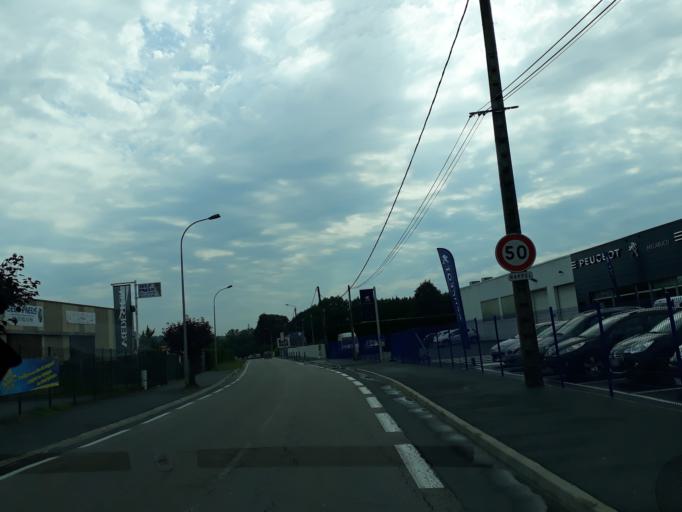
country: FR
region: Limousin
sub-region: Departement de la Correze
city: Malemort-sur-Correze
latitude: 45.1694
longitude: 1.5701
